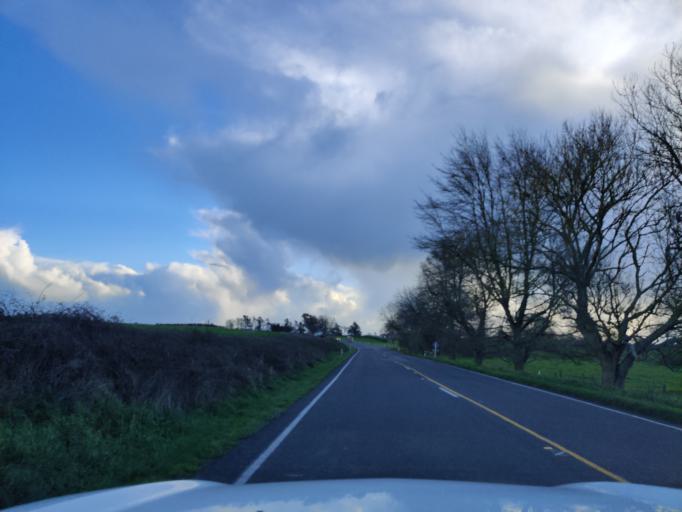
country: NZ
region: Waikato
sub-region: Waipa District
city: Cambridge
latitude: -37.6701
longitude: 175.4736
